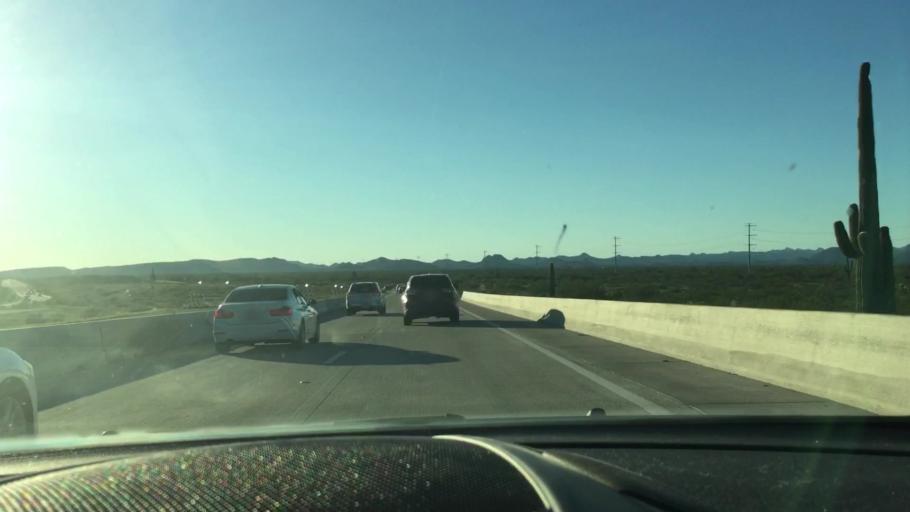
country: US
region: Arizona
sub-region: Maricopa County
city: Anthem
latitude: 33.7824
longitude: -112.1960
